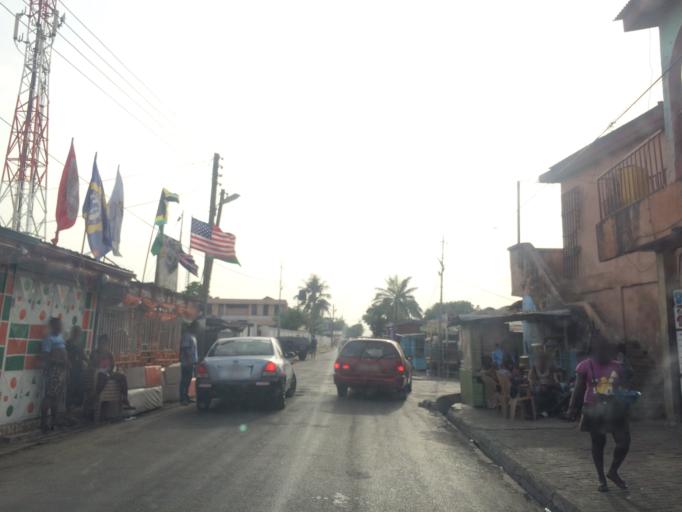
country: GH
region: Greater Accra
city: Accra
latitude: 5.5424
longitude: -0.2141
